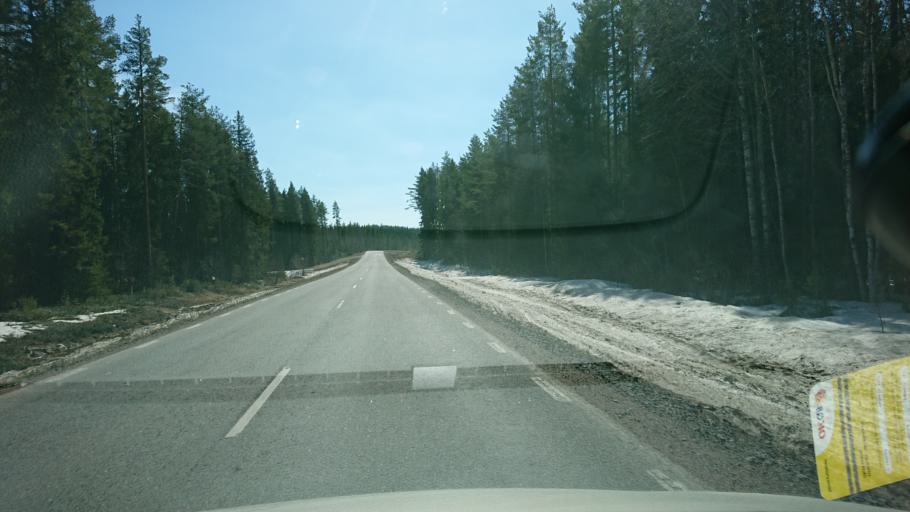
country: SE
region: Vaesternorrland
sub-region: Solleftea Kommun
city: As
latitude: 63.5893
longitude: 16.4338
